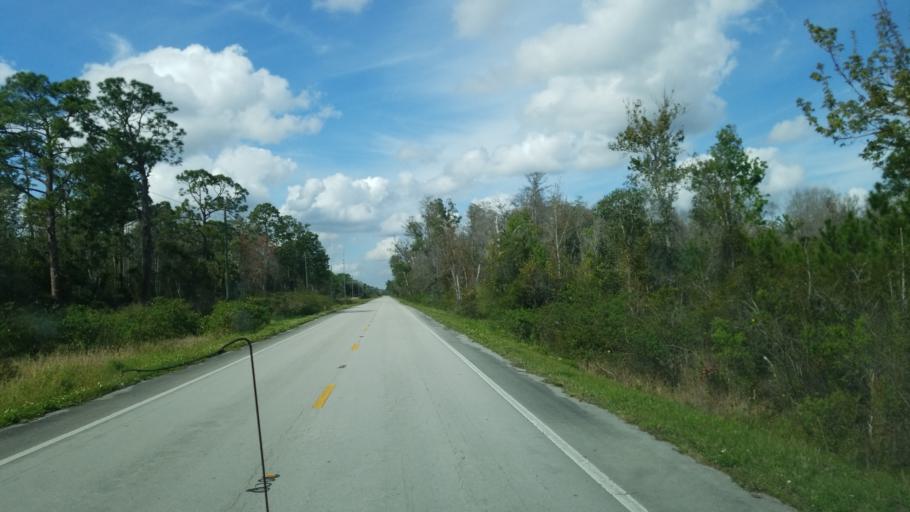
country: US
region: Florida
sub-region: Brevard County
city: June Park
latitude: 27.9870
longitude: -81.0148
